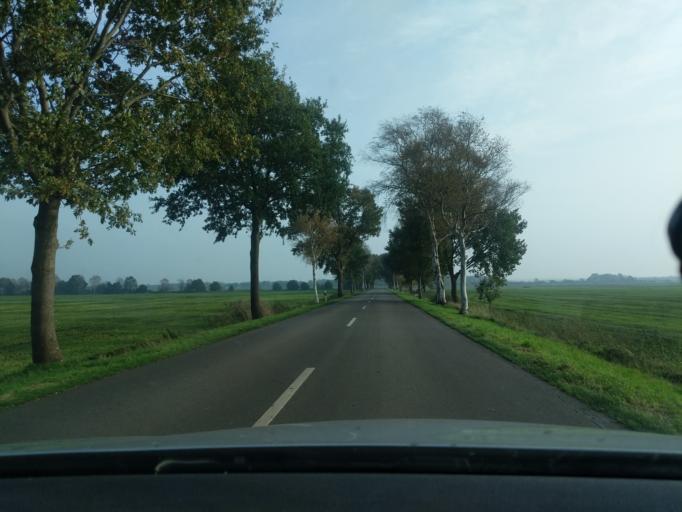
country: DE
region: Lower Saxony
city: Stinstedt
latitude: 53.6549
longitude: 8.9831
